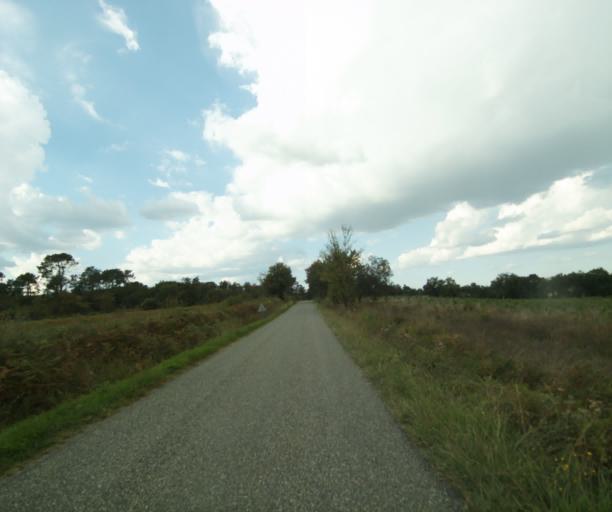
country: FR
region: Midi-Pyrenees
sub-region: Departement du Gers
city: Cazaubon
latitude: 43.8799
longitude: -0.0728
